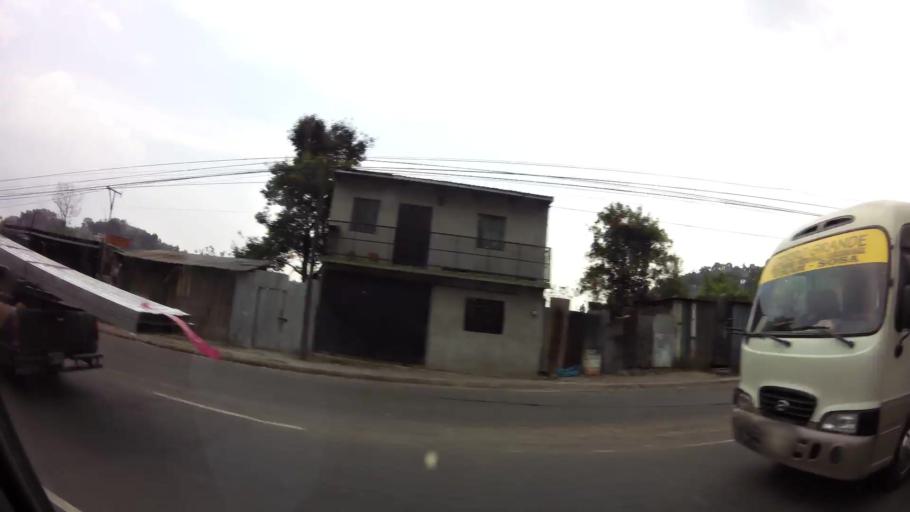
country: HN
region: Francisco Morazan
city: Tegucigalpa
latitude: 14.0851
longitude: -87.2249
